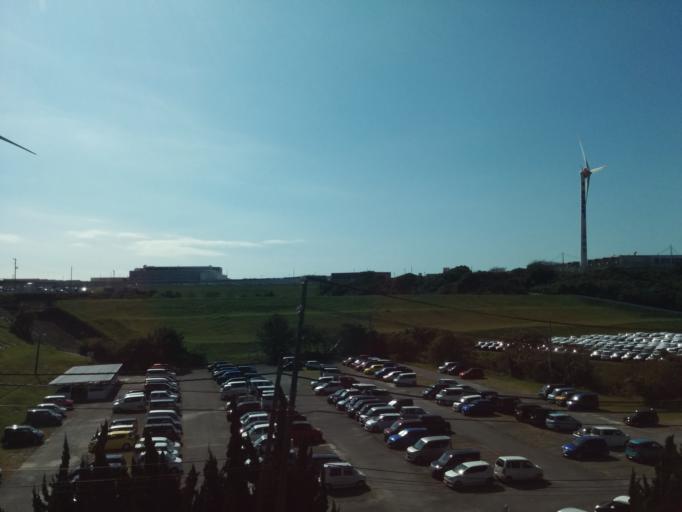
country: JP
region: Shizuoka
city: Kosai-shi
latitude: 34.7087
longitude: 137.5110
